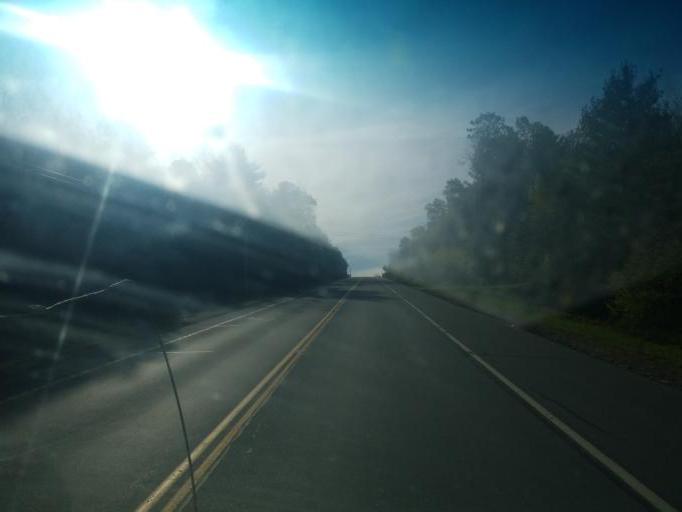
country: US
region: New Hampshire
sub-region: Grafton County
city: Deerfield
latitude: 44.2685
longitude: -71.6264
